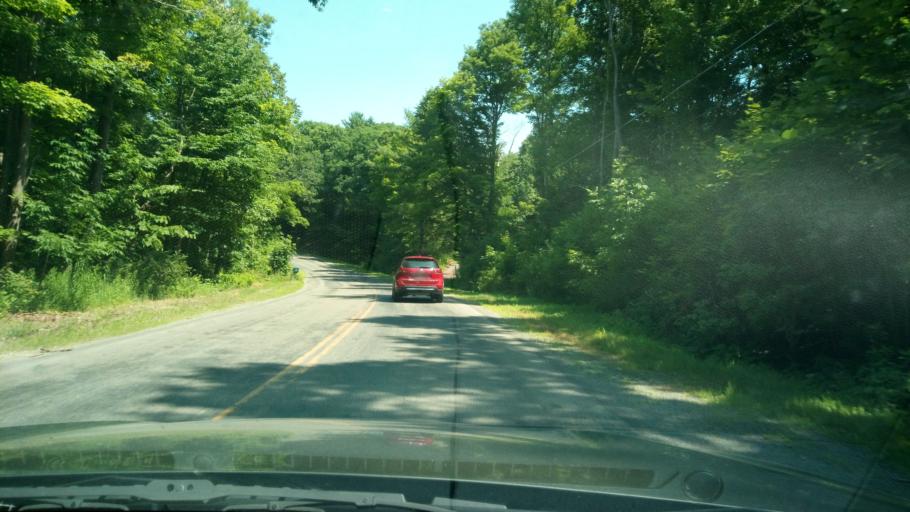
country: US
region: New York
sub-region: Chemung County
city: Horseheads North
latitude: 42.2654
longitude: -76.7994
